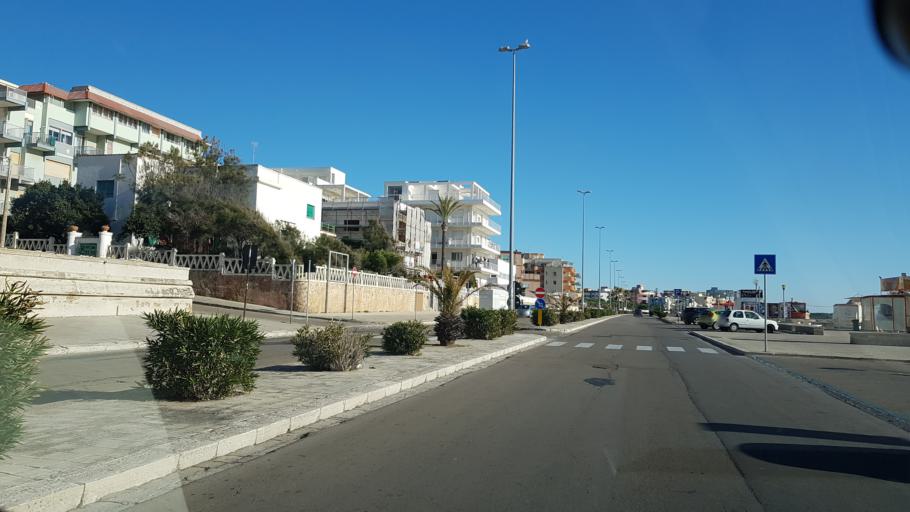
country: IT
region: Apulia
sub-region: Provincia di Lecce
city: Gallipoli
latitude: 40.0524
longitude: 17.9941
